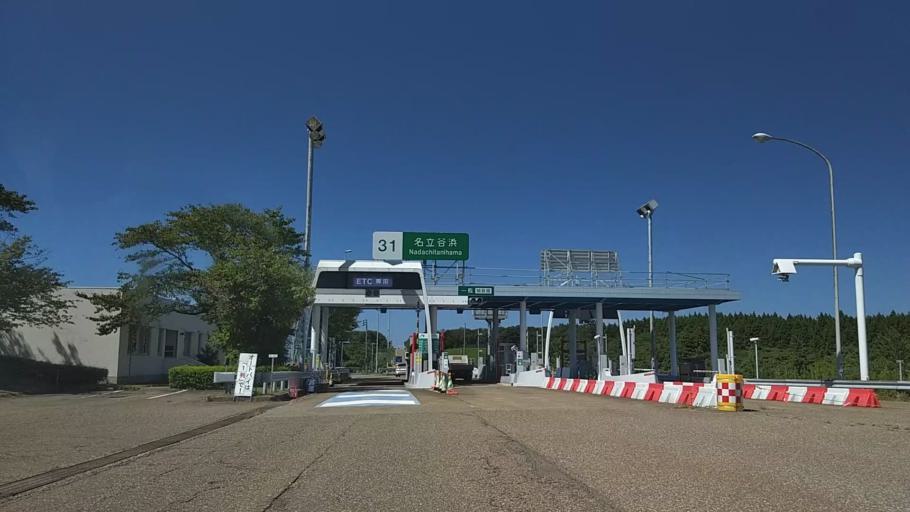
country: JP
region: Niigata
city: Joetsu
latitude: 37.1682
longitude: 138.1121
